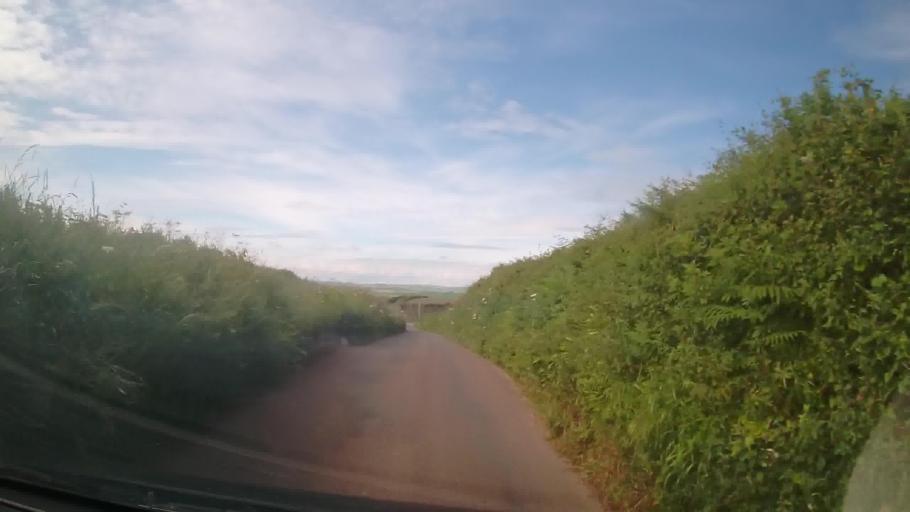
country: GB
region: England
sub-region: Devon
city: Salcombe
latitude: 50.2482
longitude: -3.6820
